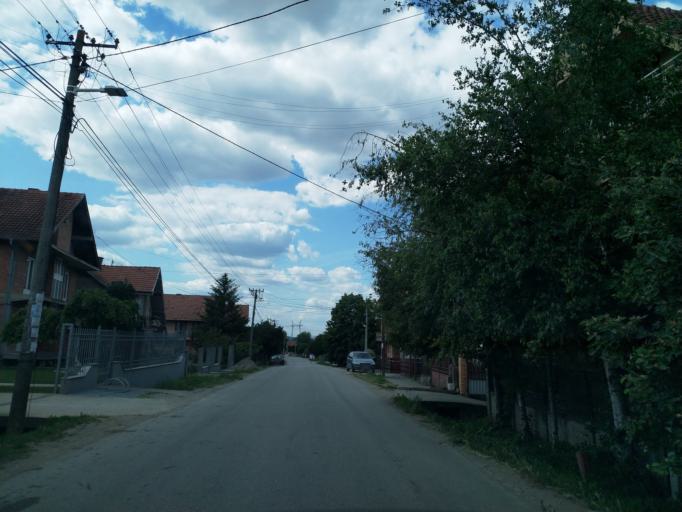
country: RS
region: Central Serbia
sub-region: Pomoravski Okrug
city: Jagodina
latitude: 43.9479
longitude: 21.2952
